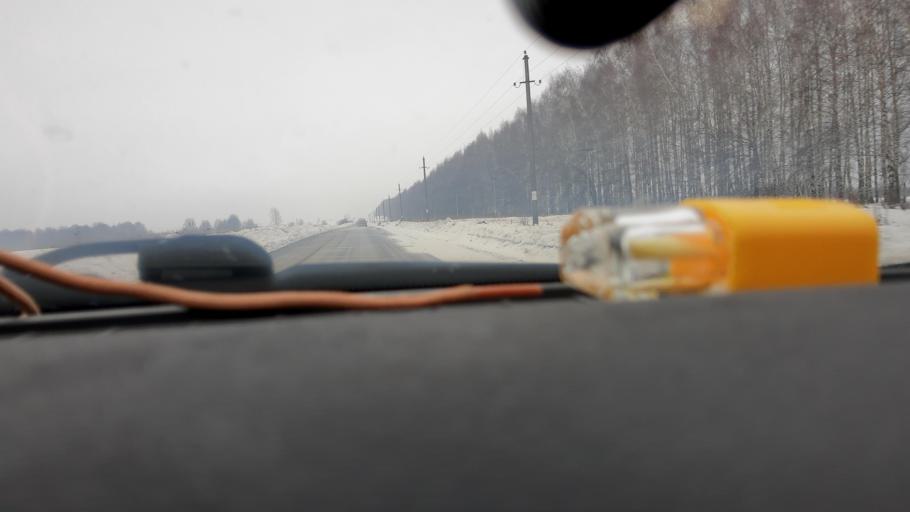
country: RU
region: Bashkortostan
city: Ulukulevo
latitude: 54.5763
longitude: 56.4276
